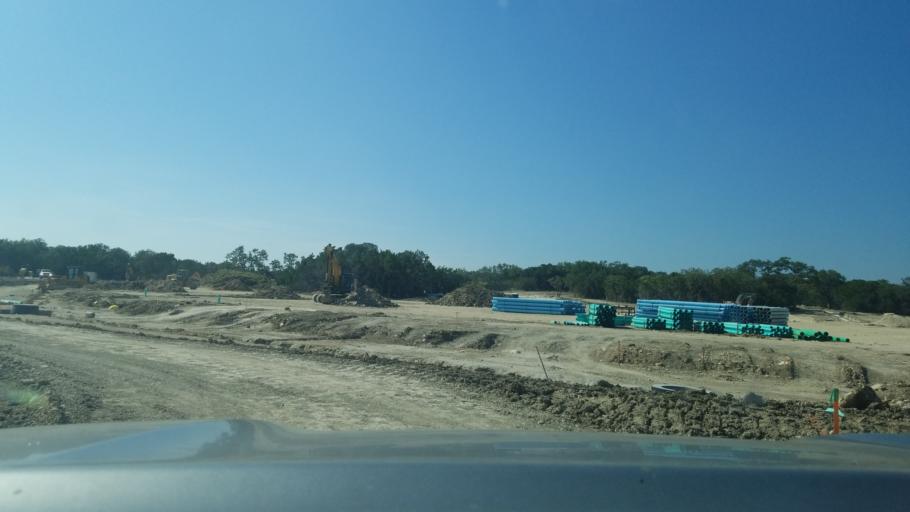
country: US
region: Texas
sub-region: Kendall County
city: Boerne
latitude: 29.7598
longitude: -98.7157
